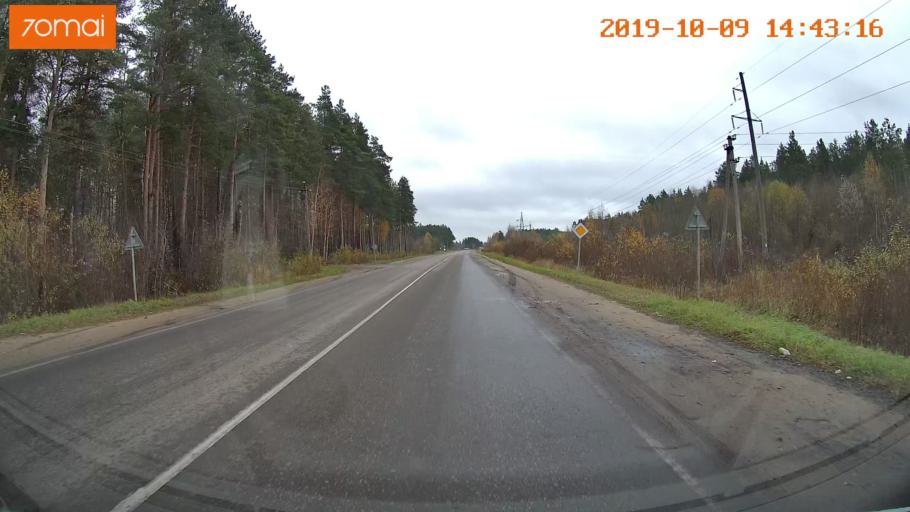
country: RU
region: Kostroma
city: Buy
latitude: 58.4582
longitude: 41.5427
